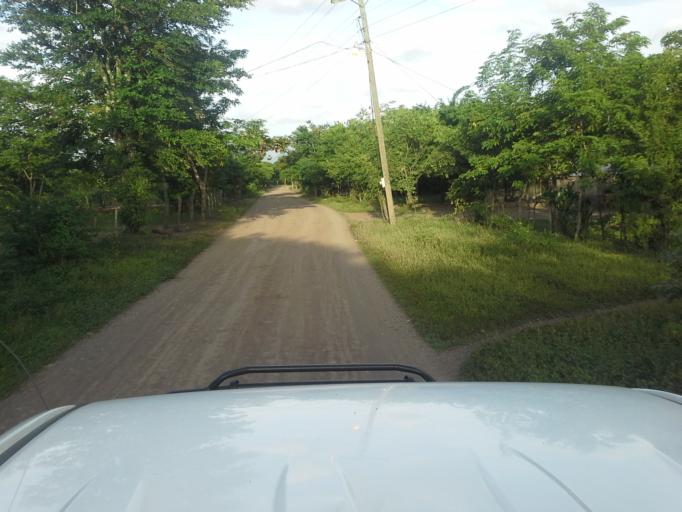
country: NI
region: Matagalpa
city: Ciudad Dario
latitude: 12.7922
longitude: -86.1545
